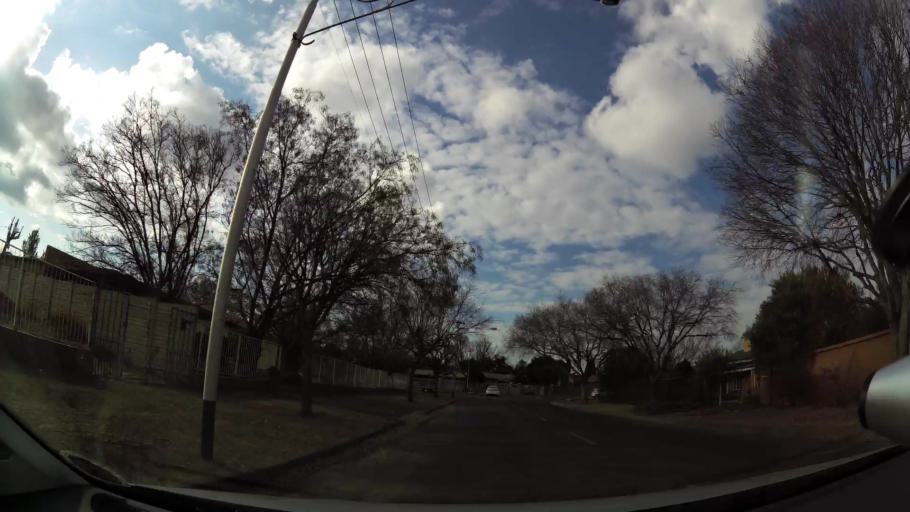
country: ZA
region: Orange Free State
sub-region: Mangaung Metropolitan Municipality
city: Bloemfontein
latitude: -29.0814
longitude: 26.2116
